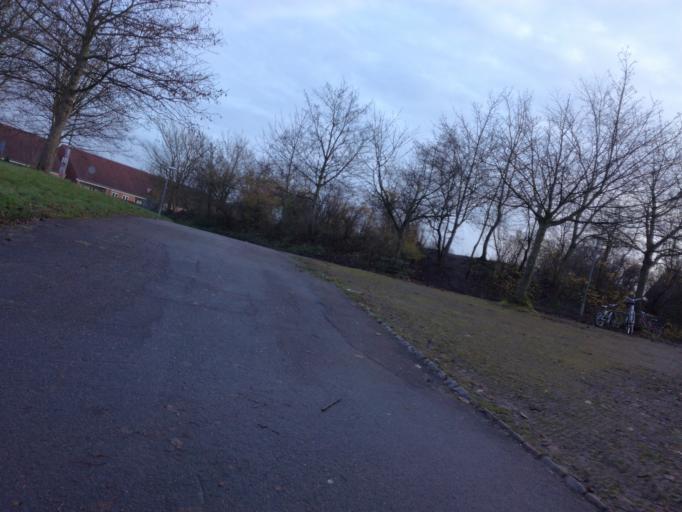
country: DK
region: South Denmark
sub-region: Vejle Kommune
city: Borkop
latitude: 55.6424
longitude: 9.6439
